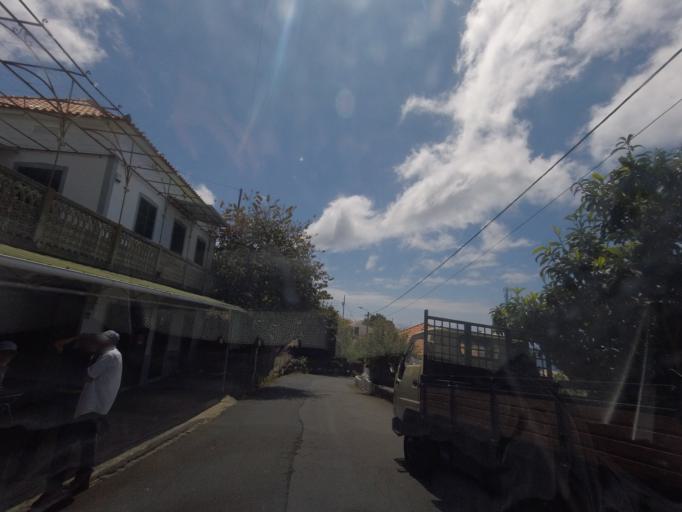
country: PT
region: Madeira
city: Ponta do Sol
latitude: 32.6798
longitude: -17.0815
